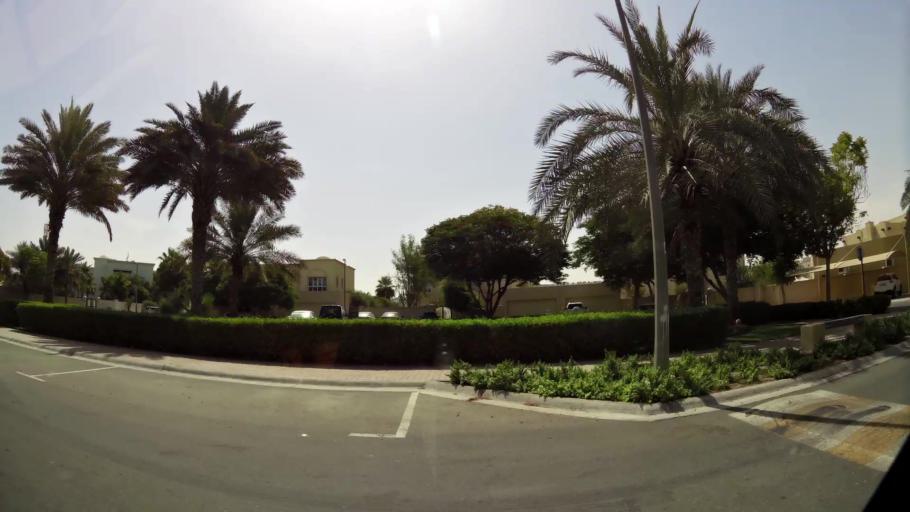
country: AE
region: Ash Shariqah
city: Sharjah
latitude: 25.1866
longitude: 55.4452
